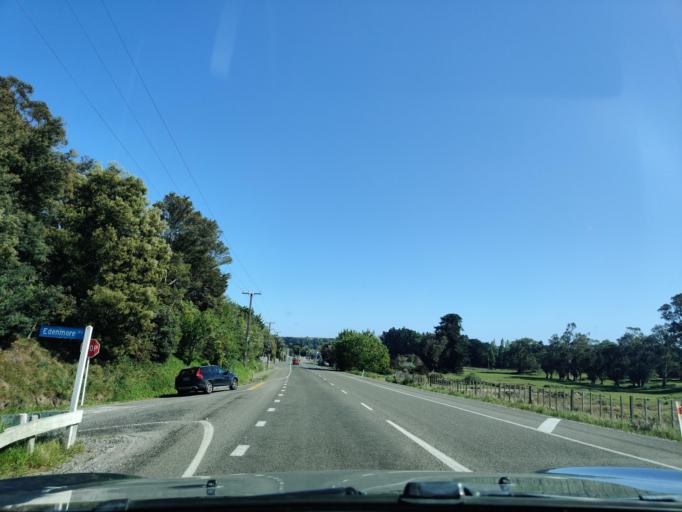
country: NZ
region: Manawatu-Wanganui
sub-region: Wanganui District
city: Wanganui
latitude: -40.0503
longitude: 175.2178
